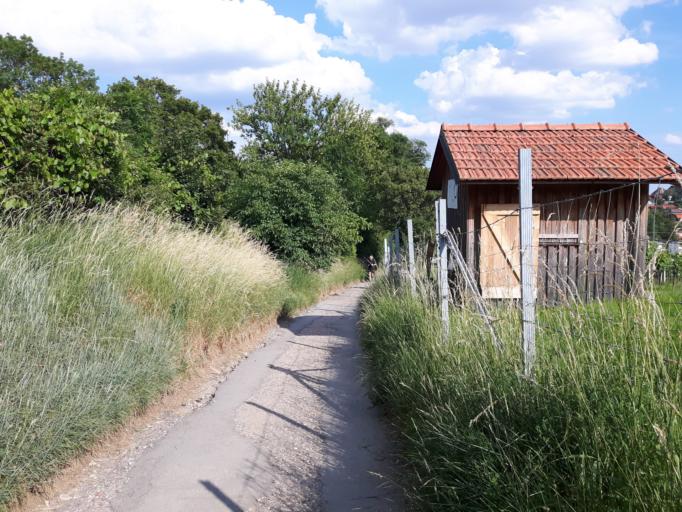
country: AT
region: Lower Austria
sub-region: Politischer Bezirk Wien-Umgebung
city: Klosterneuburg
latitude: 48.2551
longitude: 16.3101
